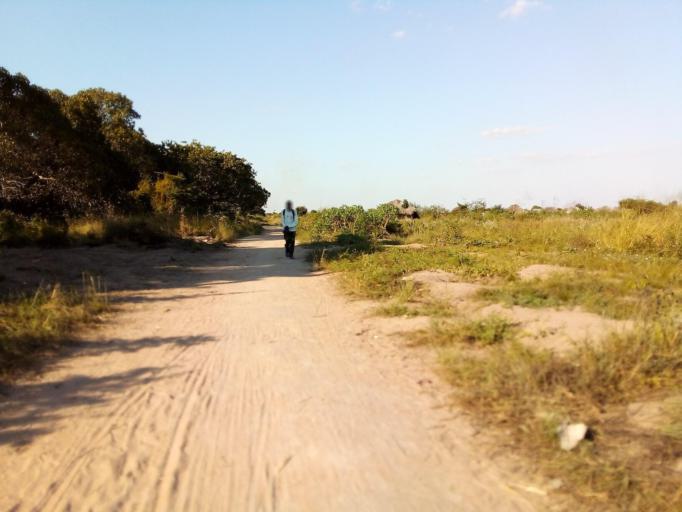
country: MZ
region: Zambezia
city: Quelimane
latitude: -17.5519
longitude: 36.7041
